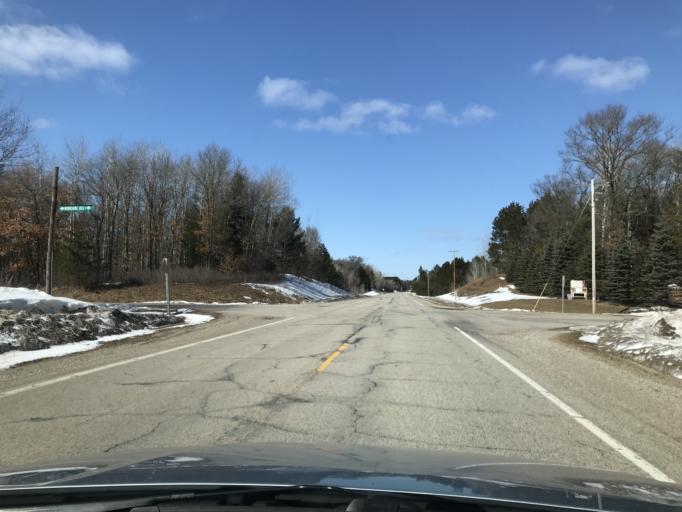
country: US
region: Wisconsin
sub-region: Marinette County
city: Peshtigo
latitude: 45.3252
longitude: -88.1020
